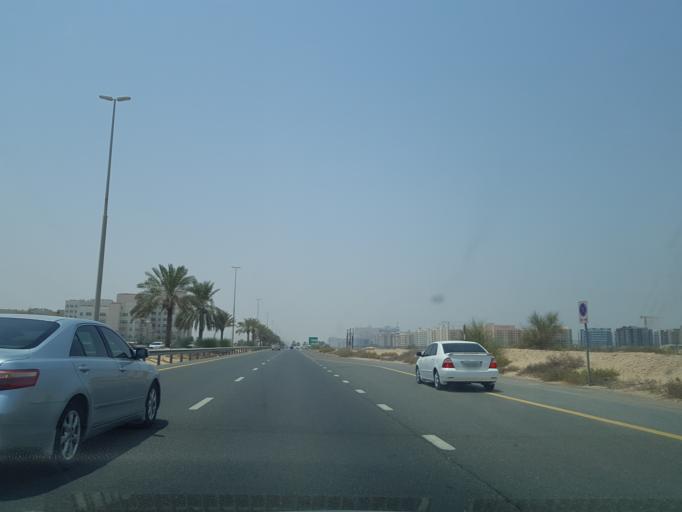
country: AE
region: Ash Shariqah
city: Sharjah
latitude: 25.1288
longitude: 55.4132
